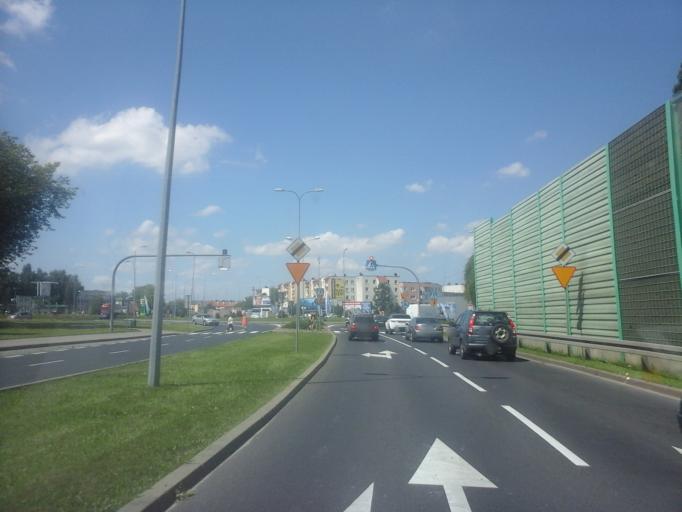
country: PL
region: West Pomeranian Voivodeship
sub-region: Koszalin
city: Koszalin
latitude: 54.1830
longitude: 16.1868
